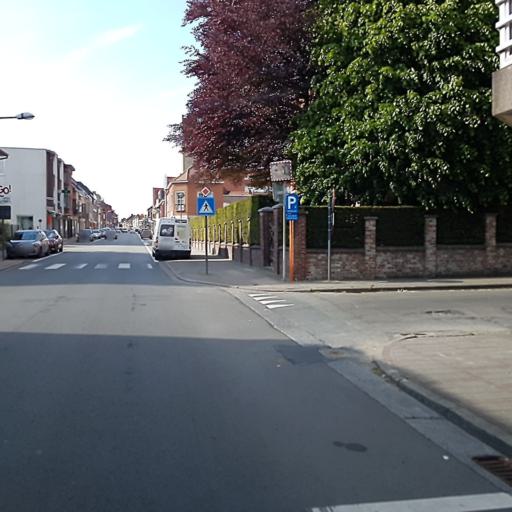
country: BE
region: Flanders
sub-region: Provincie West-Vlaanderen
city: Tielt
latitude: 50.9922
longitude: 3.3279
